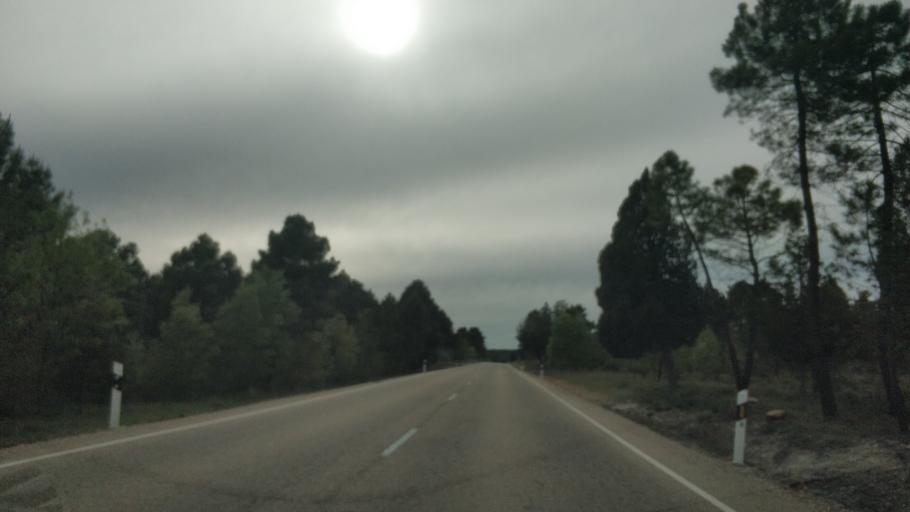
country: ES
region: Castille and Leon
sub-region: Provincia de Soria
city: Bayubas de Abajo
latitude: 41.5092
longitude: -2.9135
